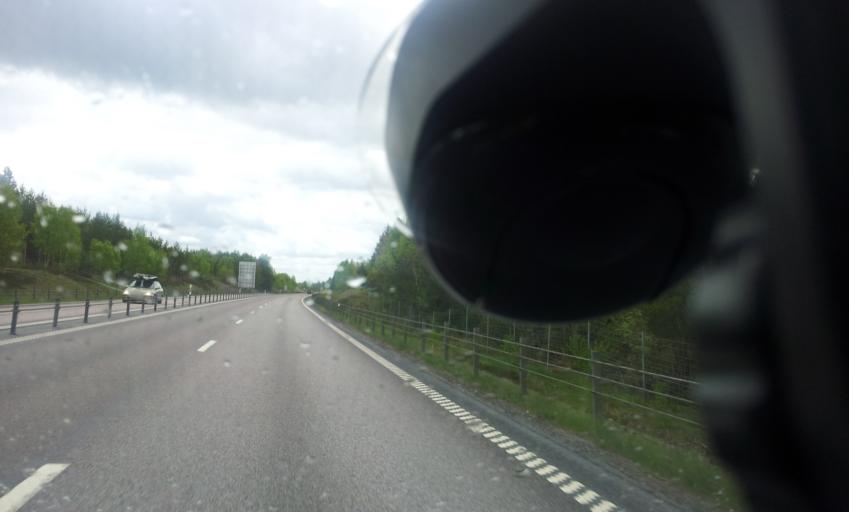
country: SE
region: Kalmar
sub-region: Oskarshamns Kommun
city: Oskarshamn
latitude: 57.2268
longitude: 16.4374
